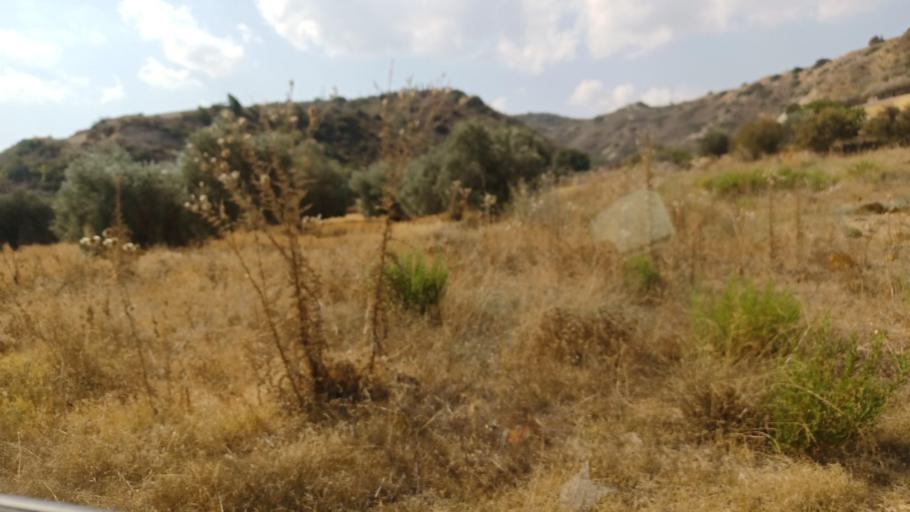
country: CY
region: Pafos
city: Polis
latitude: 34.9998
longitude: 32.4335
